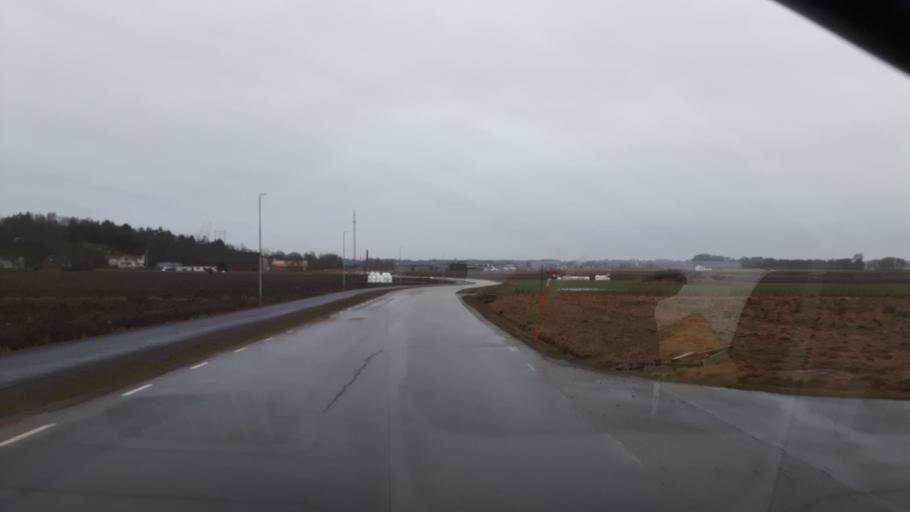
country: SE
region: Halland
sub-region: Kungsbacka Kommun
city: Frillesas
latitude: 57.3616
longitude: 12.1324
